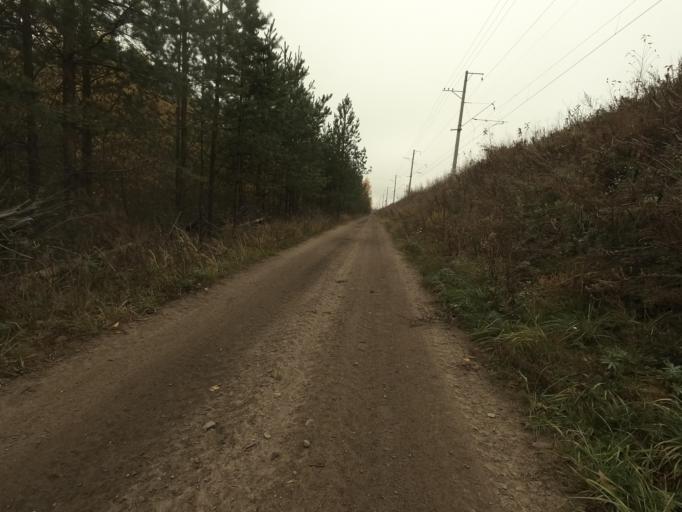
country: RU
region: Leningrad
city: Pavlovo
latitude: 59.7772
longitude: 30.9002
